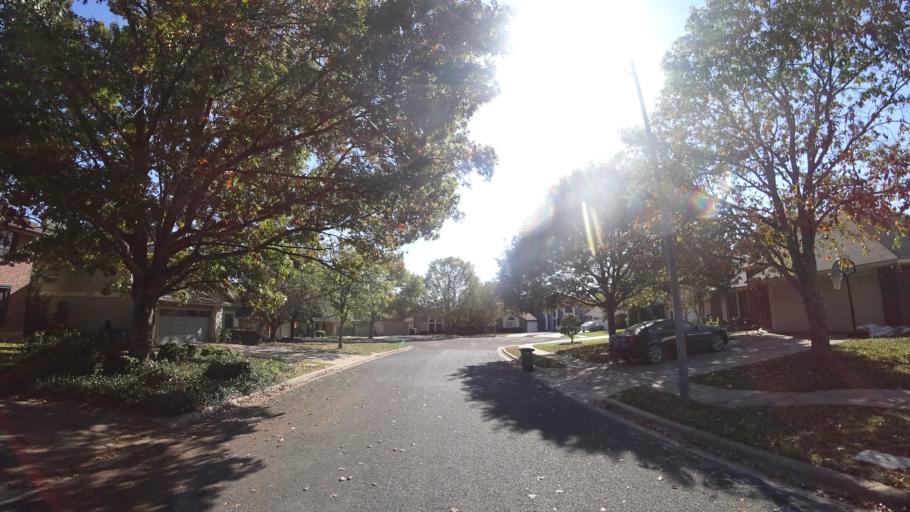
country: US
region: Texas
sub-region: Travis County
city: Shady Hollow
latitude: 30.2209
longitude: -97.8631
